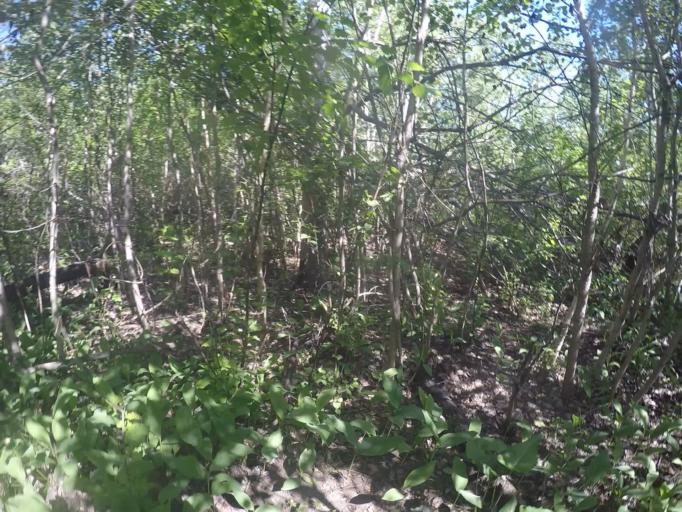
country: RU
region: Saratov
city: Krasnyy Oktyabr'
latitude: 51.3085
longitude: 45.5811
